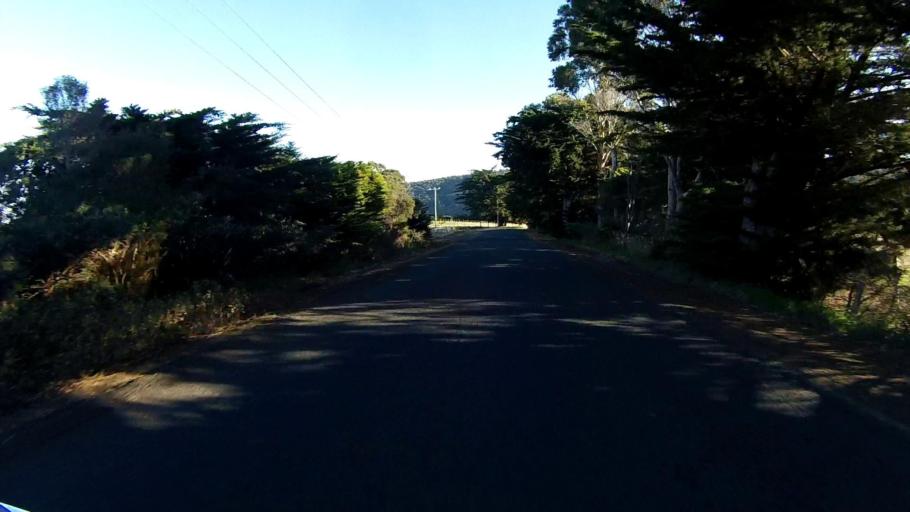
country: AU
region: Tasmania
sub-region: Clarence
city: Sandford
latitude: -43.1703
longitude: 147.8565
